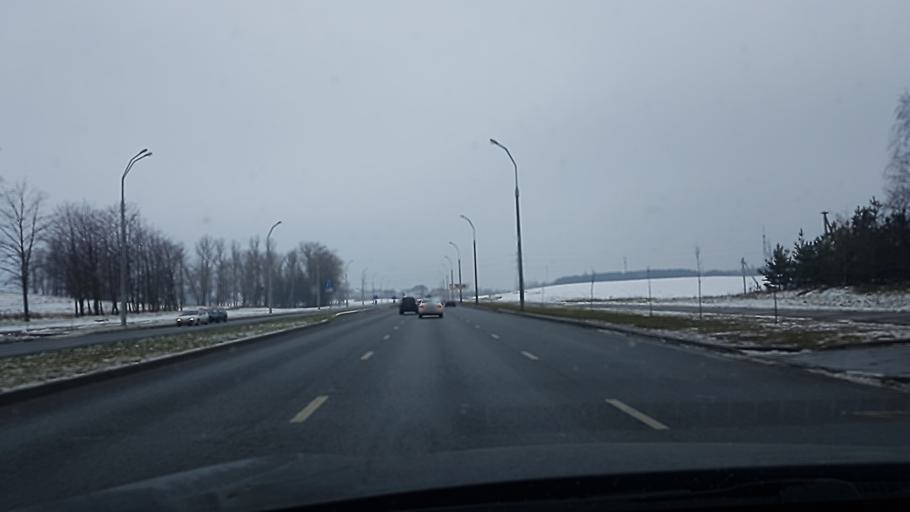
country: BY
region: Minsk
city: Minsk
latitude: 53.9446
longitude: 27.5396
